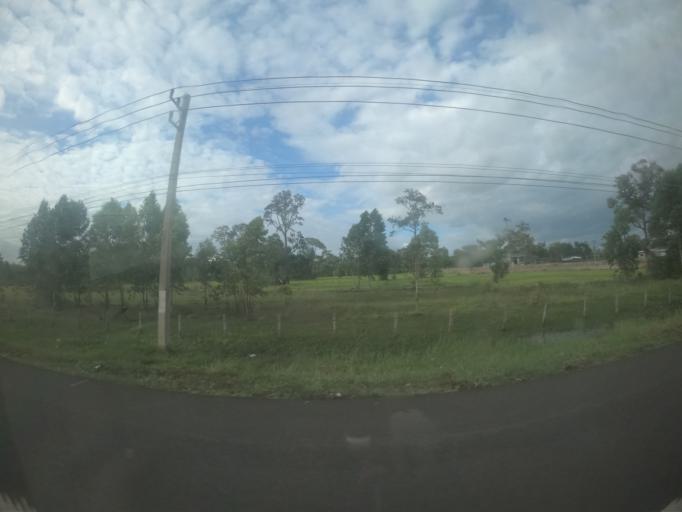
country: TH
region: Surin
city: Prasat
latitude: 14.6008
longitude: 103.4338
